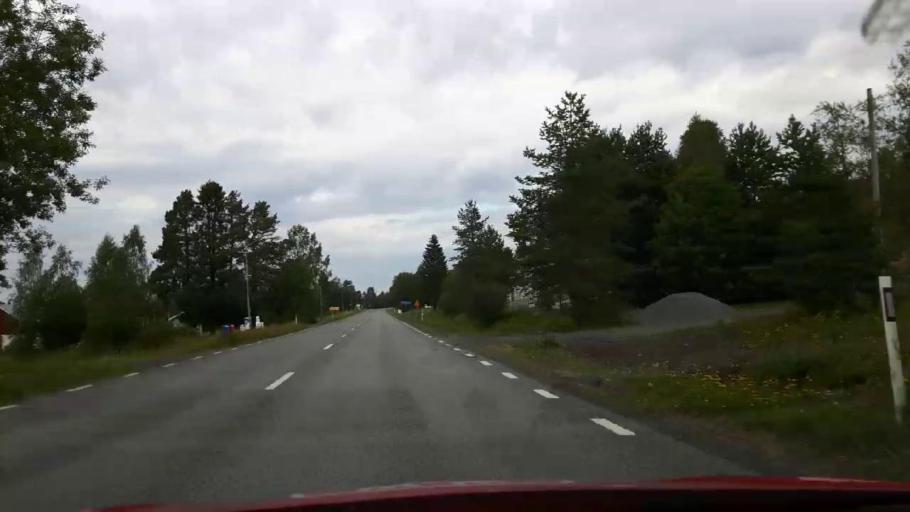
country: SE
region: Jaemtland
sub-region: Stroemsunds Kommun
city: Stroemsund
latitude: 63.5729
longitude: 15.3575
